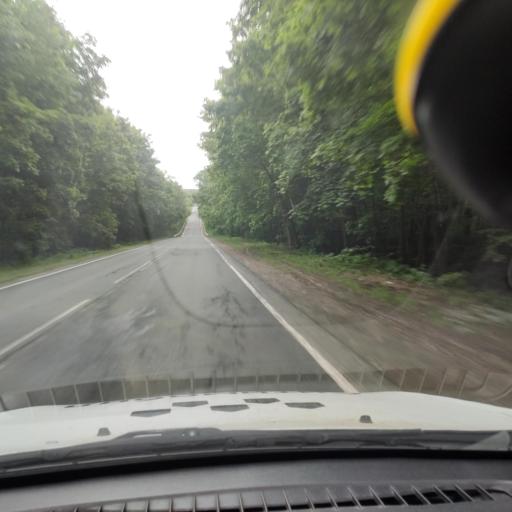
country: RU
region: Samara
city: Zhigulevsk
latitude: 53.3393
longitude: 49.4955
